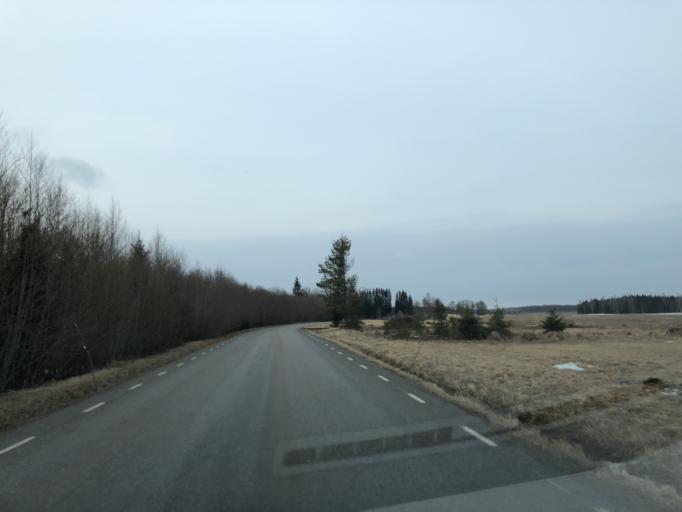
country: EE
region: Paernumaa
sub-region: Vaendra vald (alev)
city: Vandra
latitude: 58.6971
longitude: 24.9345
